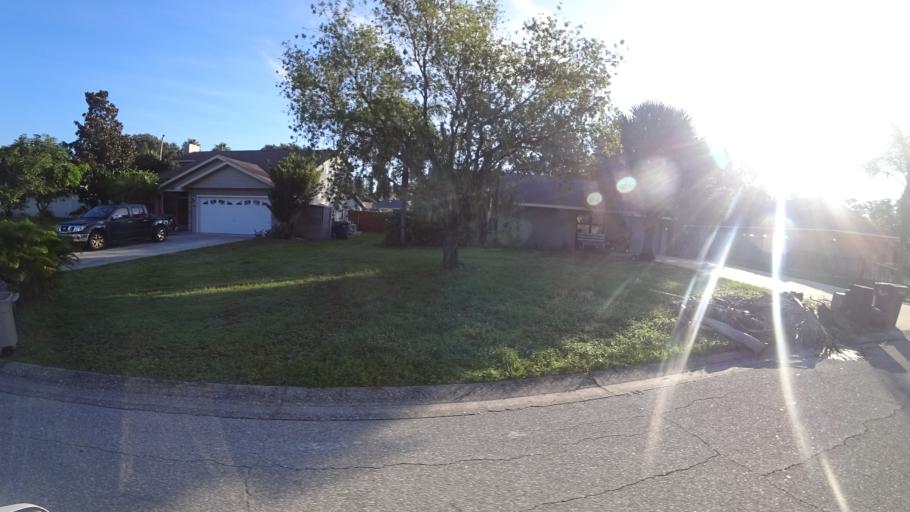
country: US
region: Florida
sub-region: Manatee County
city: Samoset
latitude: 27.4554
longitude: -82.5244
